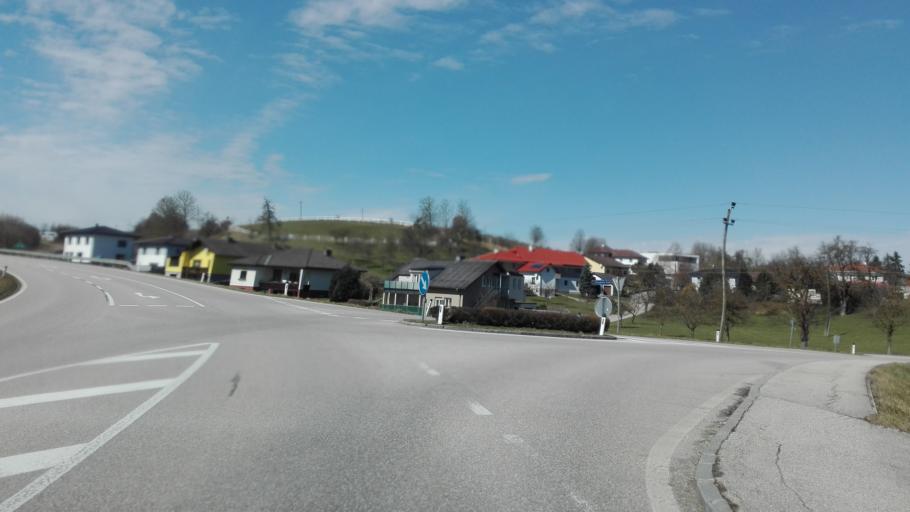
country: AT
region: Upper Austria
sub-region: Politischer Bezirk Grieskirchen
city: Bad Schallerbach
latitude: 48.1914
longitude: 13.9526
